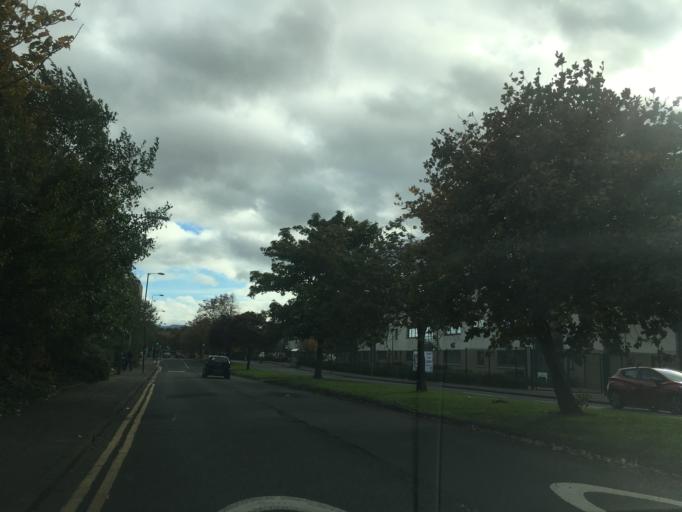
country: GB
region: Scotland
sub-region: Edinburgh
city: Edinburgh
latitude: 55.9748
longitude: -3.2536
